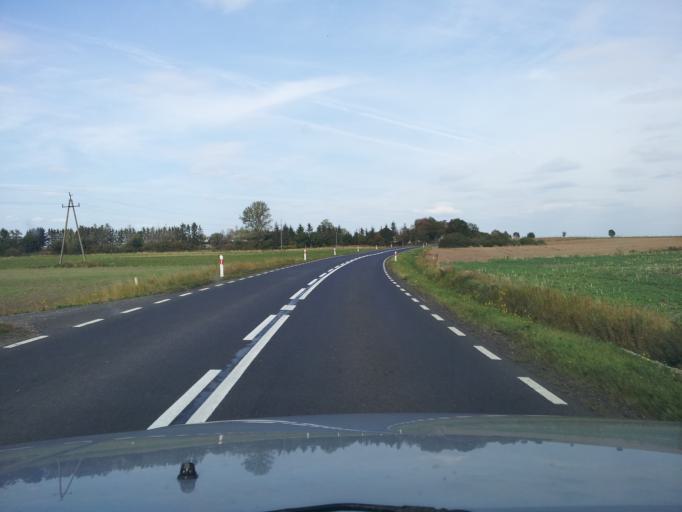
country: PL
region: Warmian-Masurian Voivodeship
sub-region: Powiat ilawski
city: Lubawa
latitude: 53.5693
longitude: 19.7846
